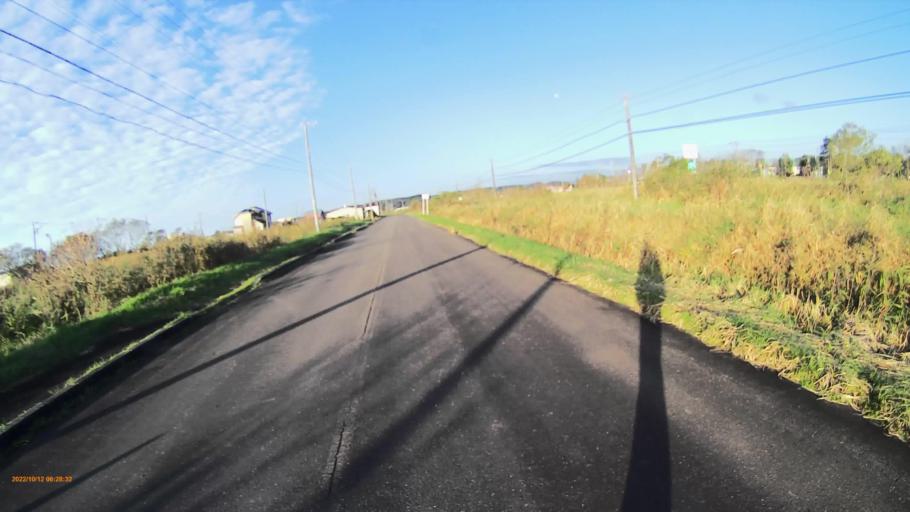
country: JP
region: Hokkaido
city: Kushiro
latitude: 42.8905
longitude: 143.9412
